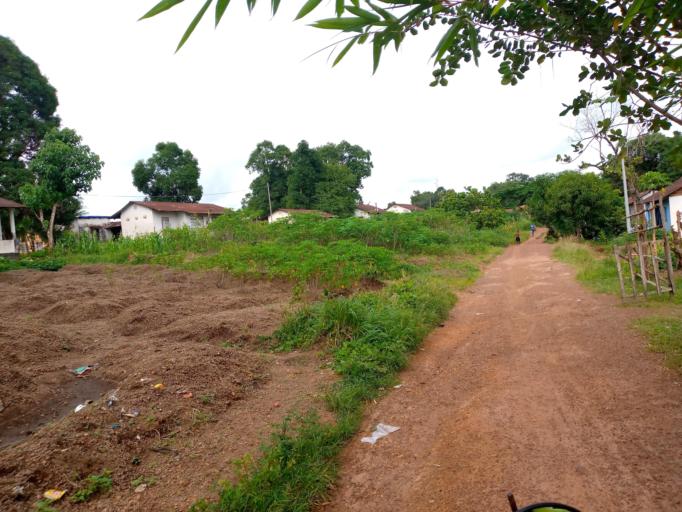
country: SL
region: Northern Province
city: Magburaka
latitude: 8.7220
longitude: -11.9426
